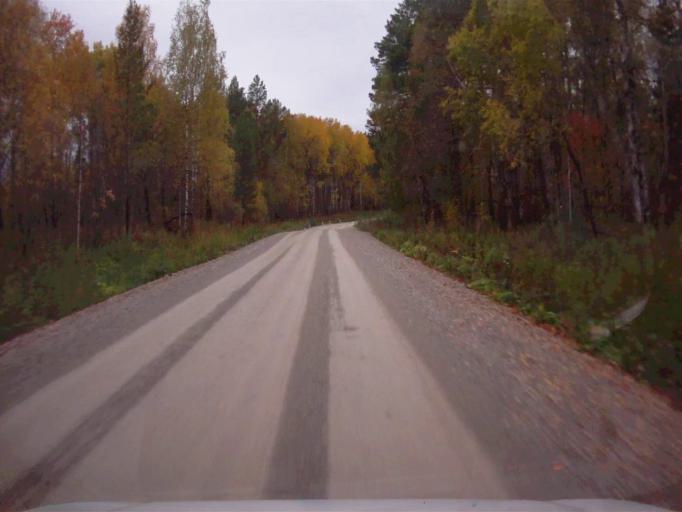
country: RU
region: Chelyabinsk
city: Nyazepetrovsk
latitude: 56.0675
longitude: 59.4356
